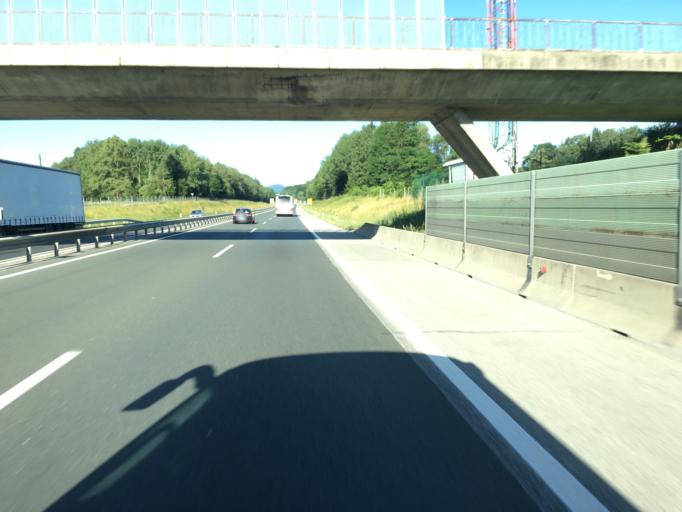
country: SI
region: Slovenska Bistrica
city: Slovenska Bistrica
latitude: 46.3748
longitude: 15.5467
